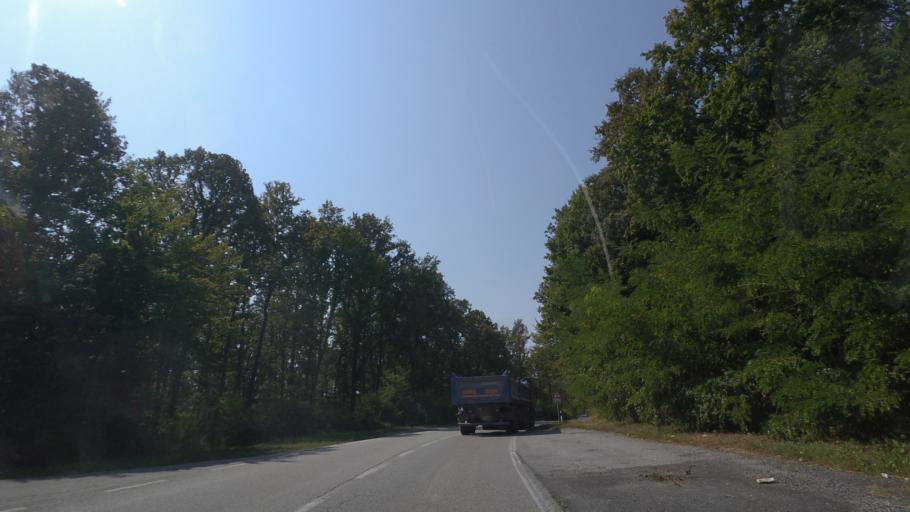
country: HR
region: Sisacko-Moslavacka
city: Novska
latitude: 45.3724
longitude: 17.0247
